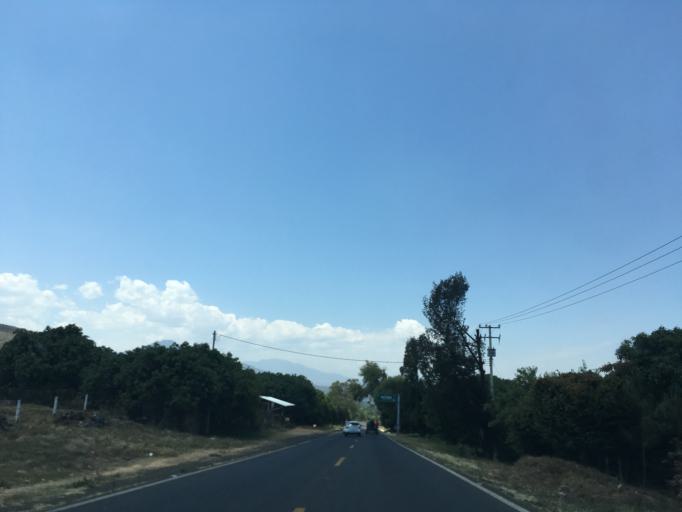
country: MX
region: Michoacan
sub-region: Chilchota
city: Tacuro (Santa Maria Tacuro)
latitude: 19.8534
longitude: -102.0458
